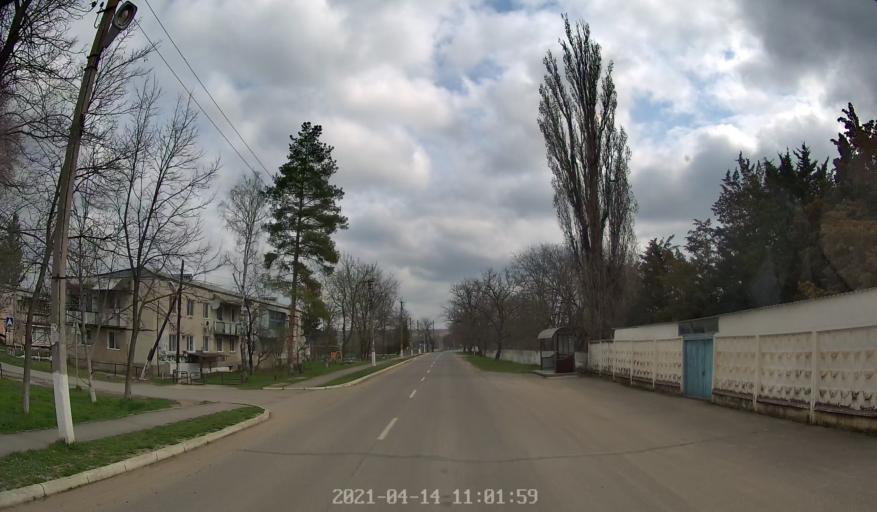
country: MD
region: Criuleni
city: Criuleni
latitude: 47.1541
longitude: 29.1475
